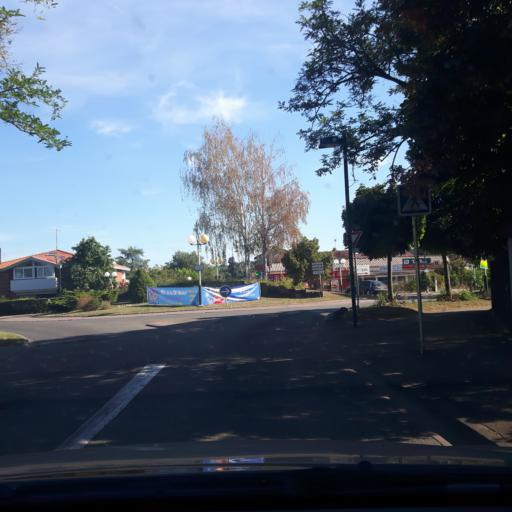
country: FR
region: Midi-Pyrenees
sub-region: Departement de la Haute-Garonne
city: Villemur-sur-Tarn
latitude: 43.8583
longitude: 1.5013
